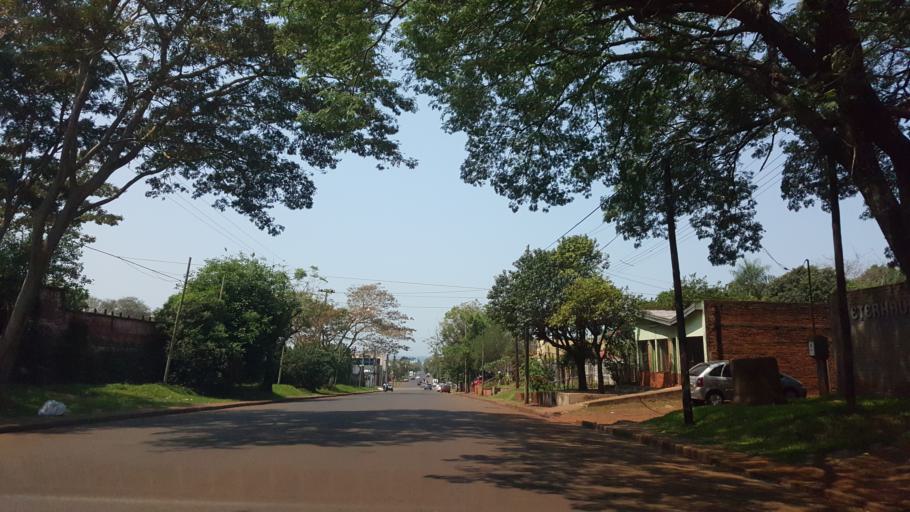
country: AR
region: Misiones
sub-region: Departamento de Capital
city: Posadas
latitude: -27.3829
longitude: -55.9131
